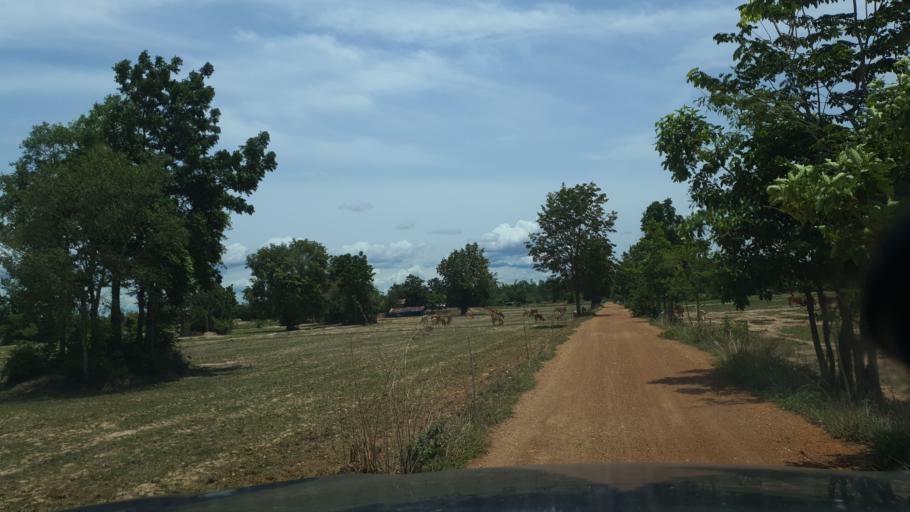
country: TH
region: Sukhothai
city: Ban Na
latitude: 17.1478
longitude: 99.6685
